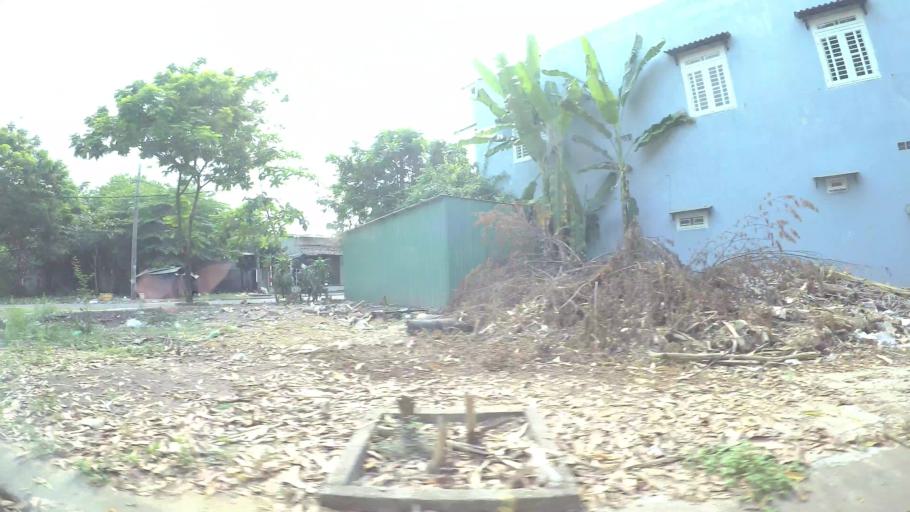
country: VN
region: Da Nang
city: Lien Chieu
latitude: 16.0573
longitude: 108.1607
